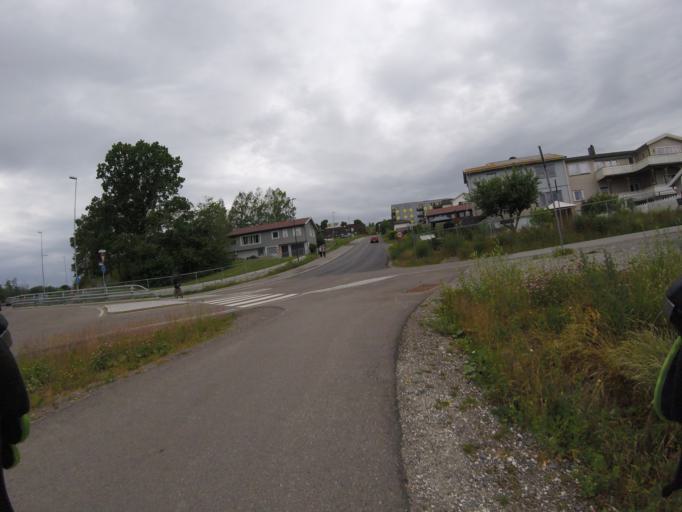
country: NO
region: Akershus
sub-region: Skedsmo
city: Lillestrom
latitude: 59.9760
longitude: 11.0258
